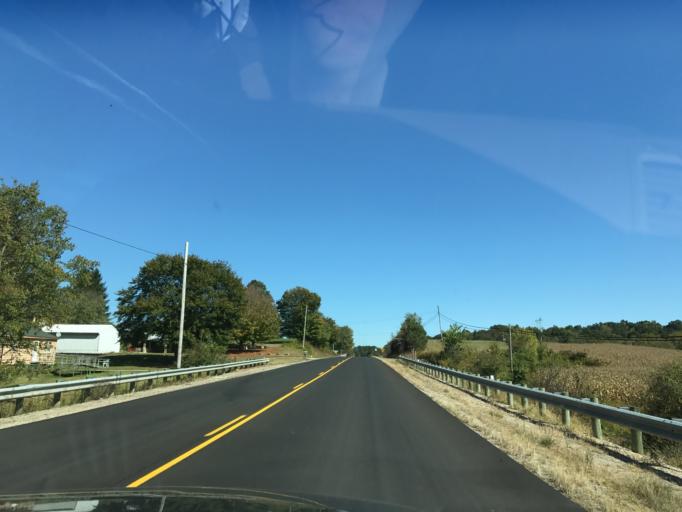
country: US
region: Ohio
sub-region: Muskingum County
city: Pleasant Grove
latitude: 39.9716
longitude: -81.8552
